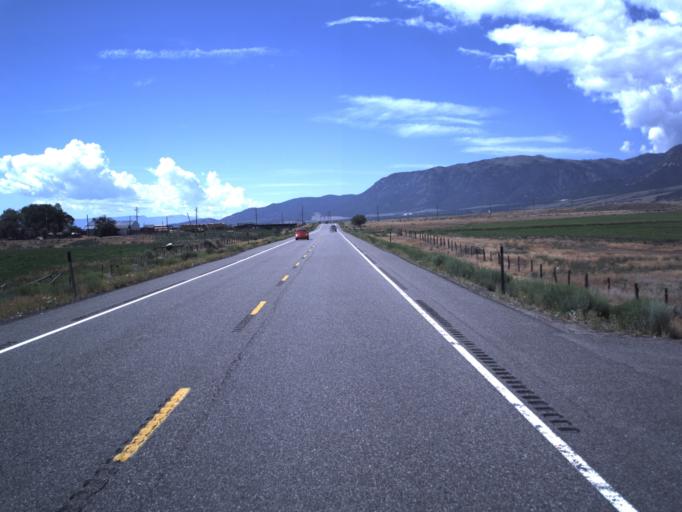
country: US
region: Utah
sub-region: Piute County
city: Junction
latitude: 38.4366
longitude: -112.2306
